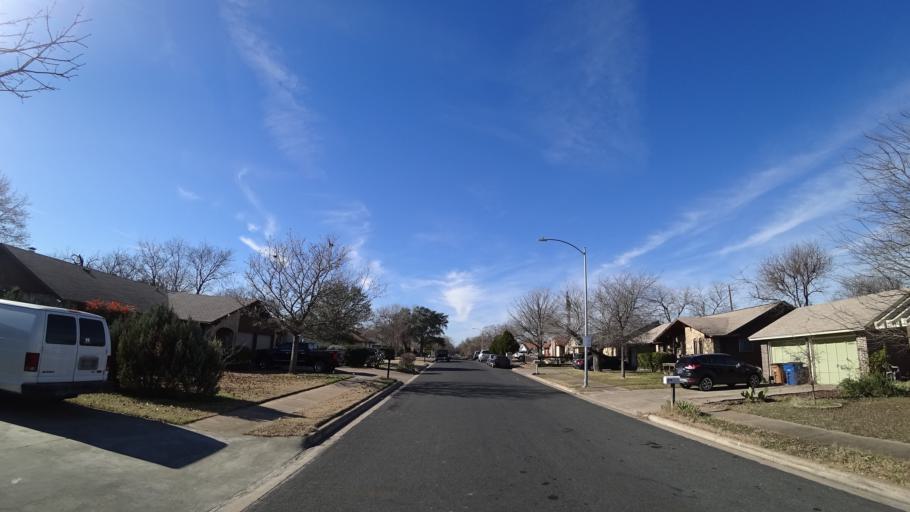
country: US
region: Texas
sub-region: Travis County
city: Wells Branch
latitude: 30.3800
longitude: -97.7025
